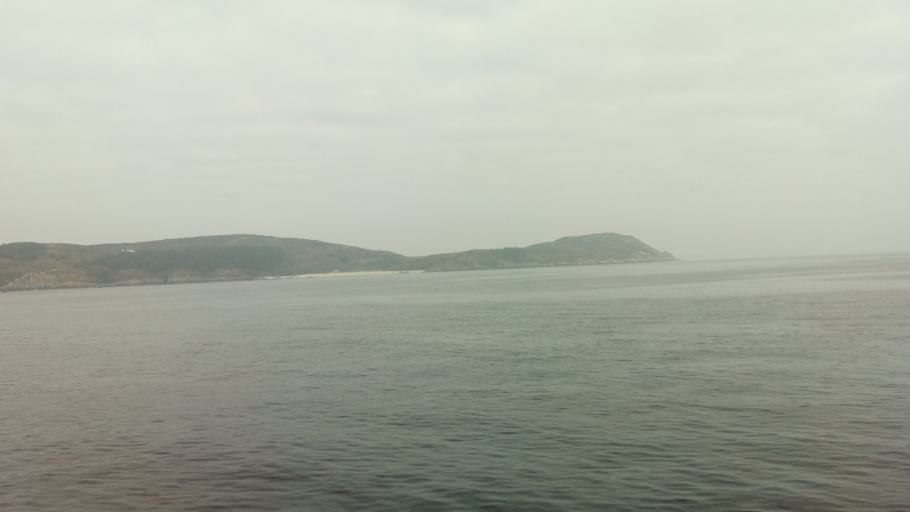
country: ES
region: Galicia
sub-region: Provincia de Pontevedra
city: Sanxenxo
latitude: 42.3788
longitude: -8.9155
